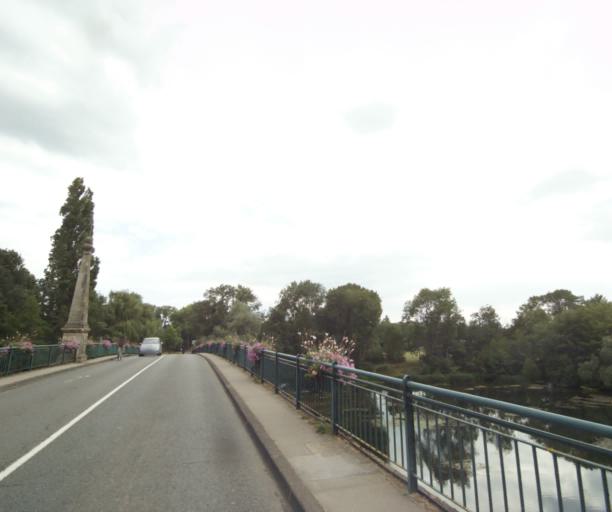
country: FR
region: Centre
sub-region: Departement du Loiret
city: Saint-Hilaire-Saint-Mesmin
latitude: 47.8728
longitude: 1.8400
